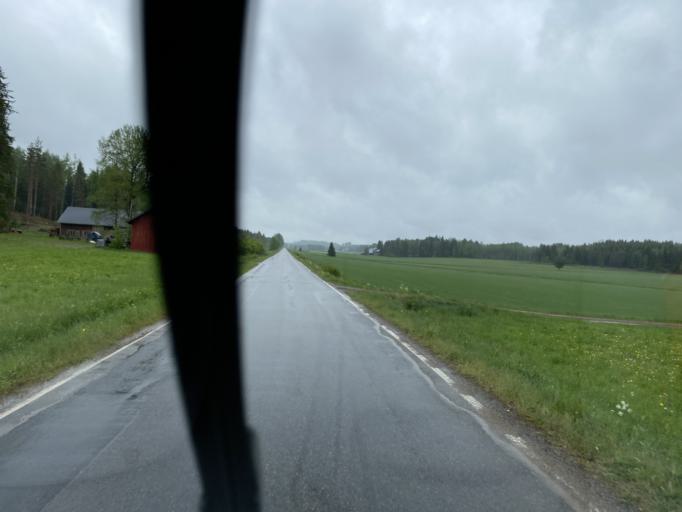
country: FI
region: Haeme
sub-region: Forssa
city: Humppila
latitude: 61.0473
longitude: 23.3701
